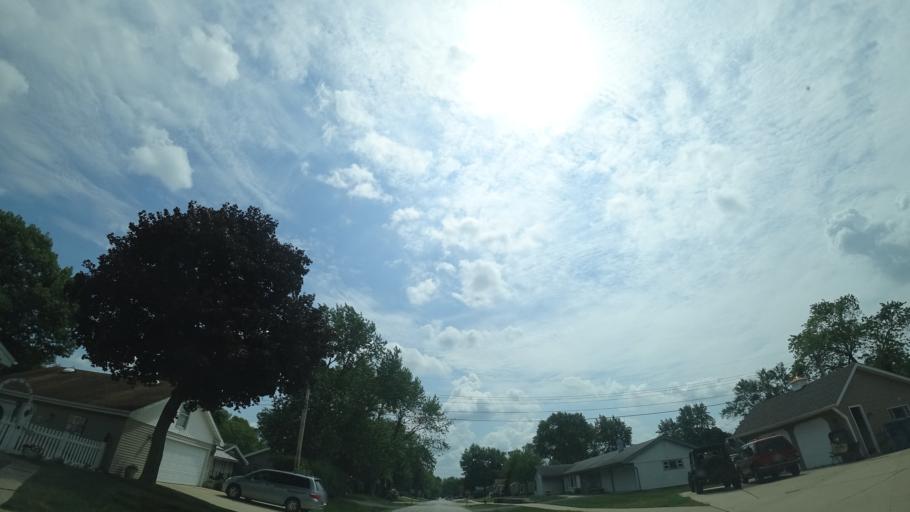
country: US
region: Illinois
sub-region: Cook County
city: Worth
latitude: 41.6871
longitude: -87.7914
